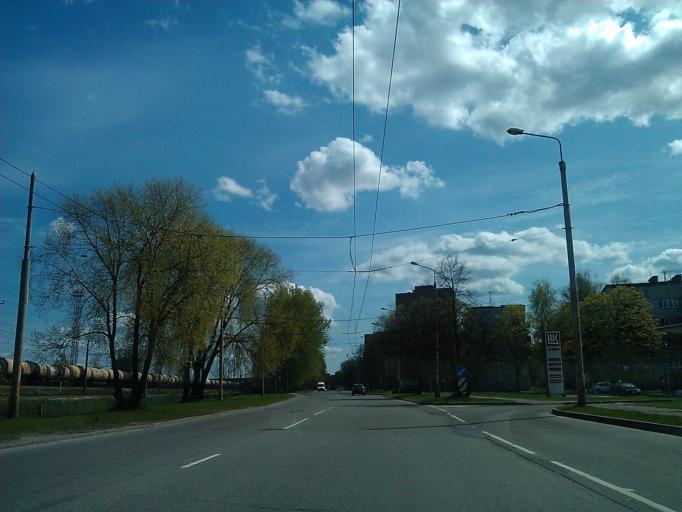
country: LV
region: Kekava
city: Balozi
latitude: 56.9231
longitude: 24.1798
